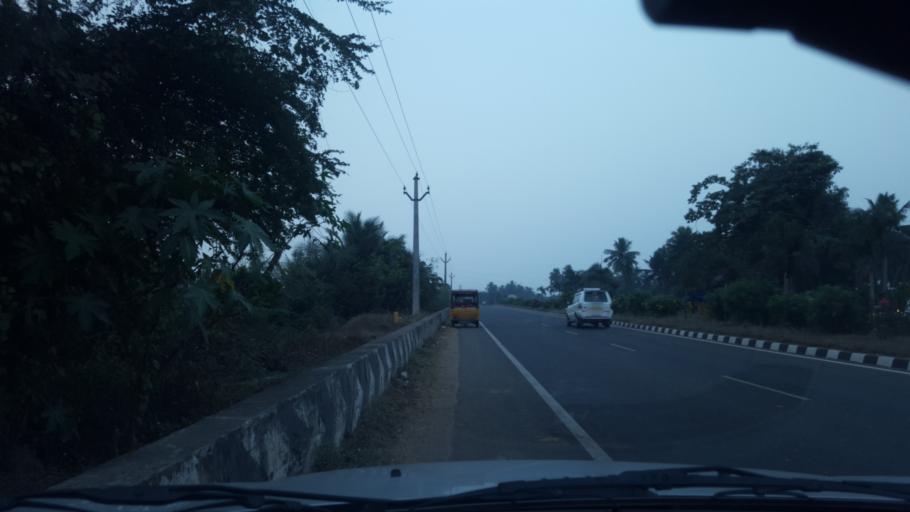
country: IN
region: Andhra Pradesh
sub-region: East Godavari
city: Rajahmundry
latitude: 16.9189
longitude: 81.7912
